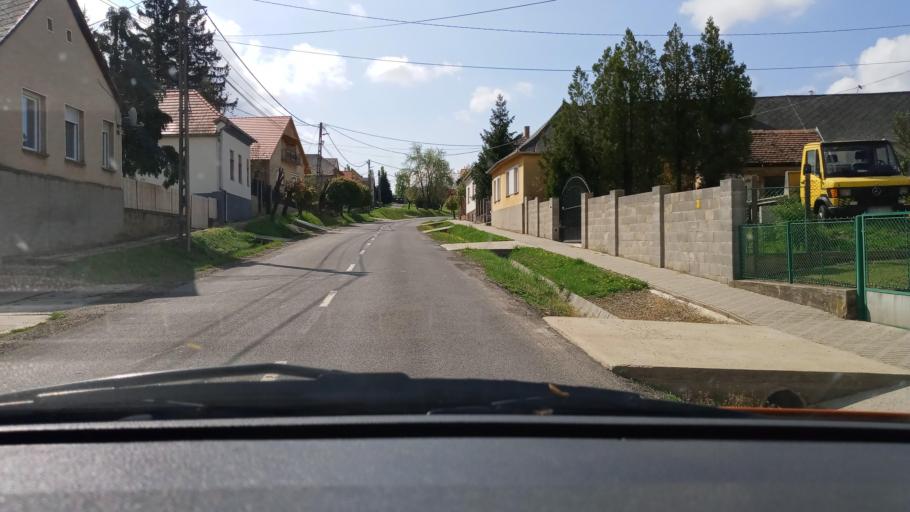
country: HU
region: Baranya
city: Hosszuheteny
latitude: 46.1550
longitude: 18.3557
